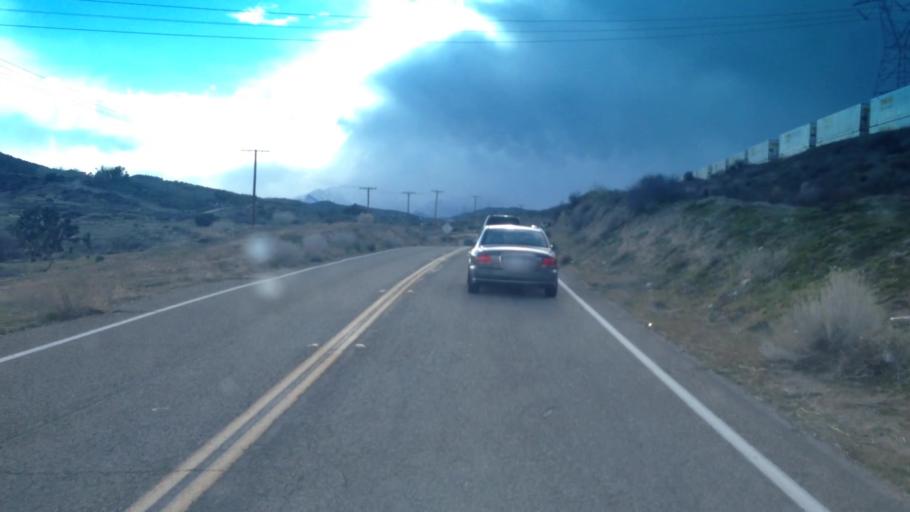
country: US
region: California
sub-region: San Bernardino County
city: Oak Hills
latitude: 34.3625
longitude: -117.3571
